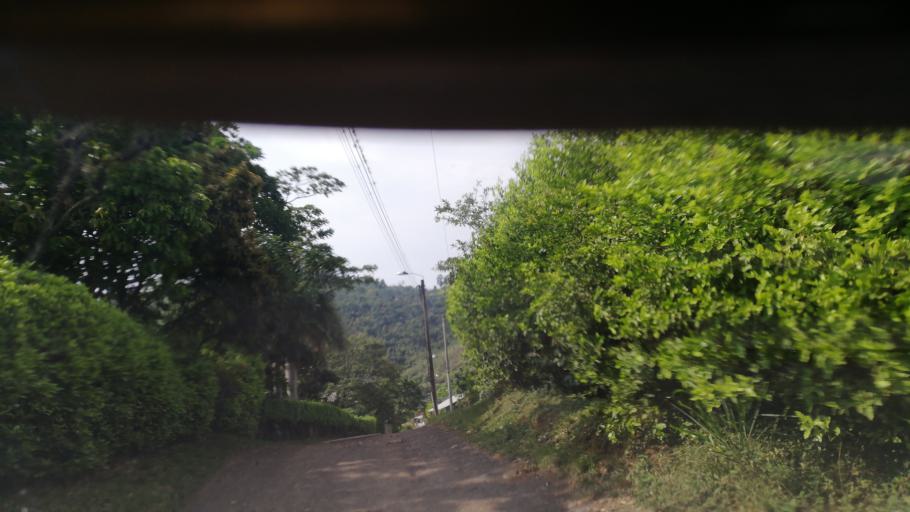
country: CO
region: Valle del Cauca
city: Cali
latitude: 3.4979
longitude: -76.5471
